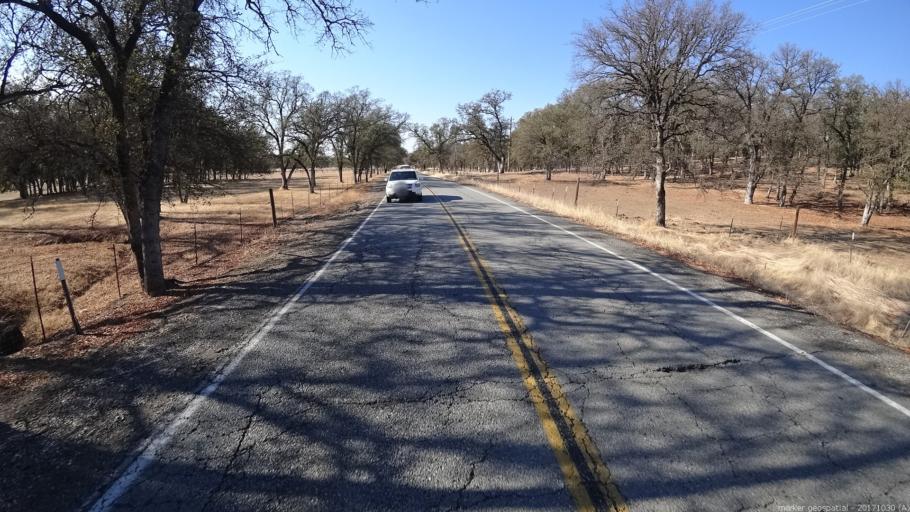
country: US
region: California
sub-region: Shasta County
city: Bella Vista
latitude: 40.6006
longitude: -122.1654
